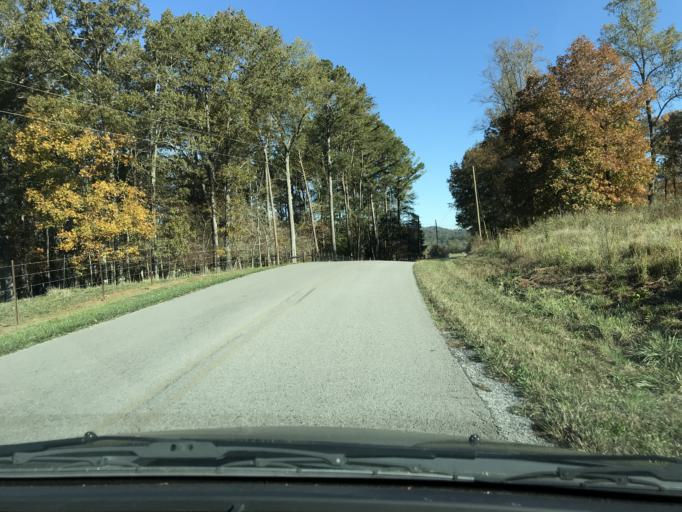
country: US
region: Georgia
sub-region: Dade County
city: Trenton
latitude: 34.8906
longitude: -85.4689
